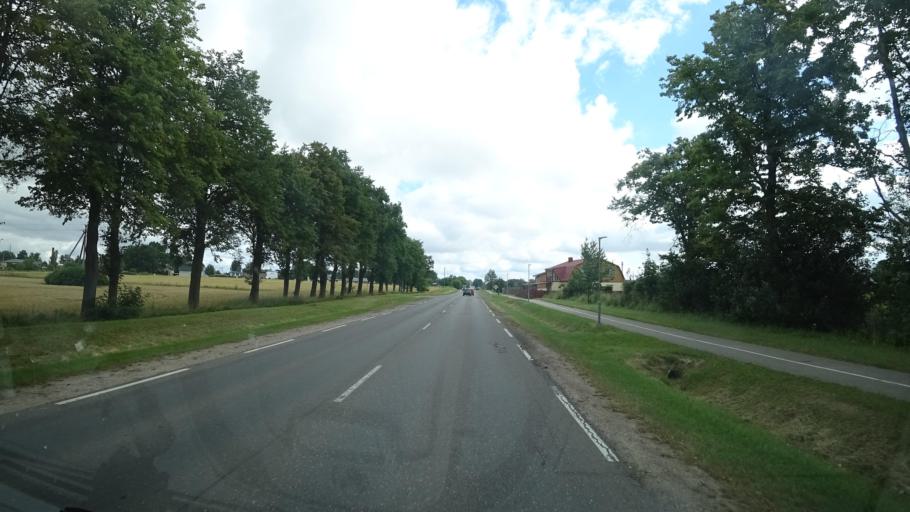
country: LT
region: Marijampoles apskritis
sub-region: Marijampole Municipality
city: Marijampole
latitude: 54.5306
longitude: 23.3310
